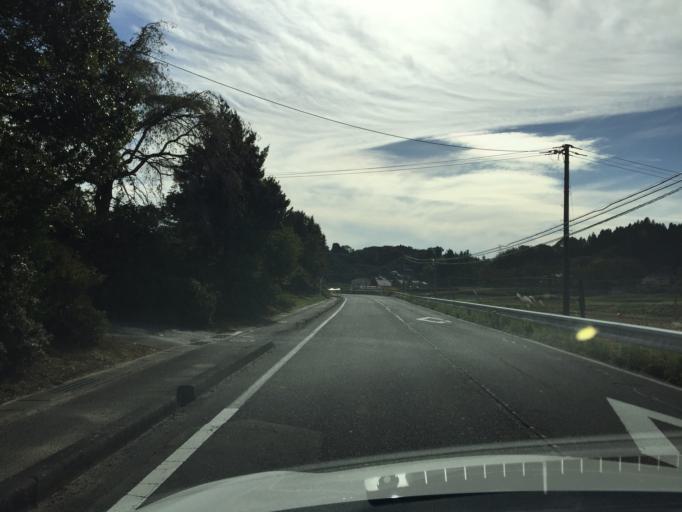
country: JP
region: Fukushima
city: Miharu
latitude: 37.4221
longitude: 140.4618
